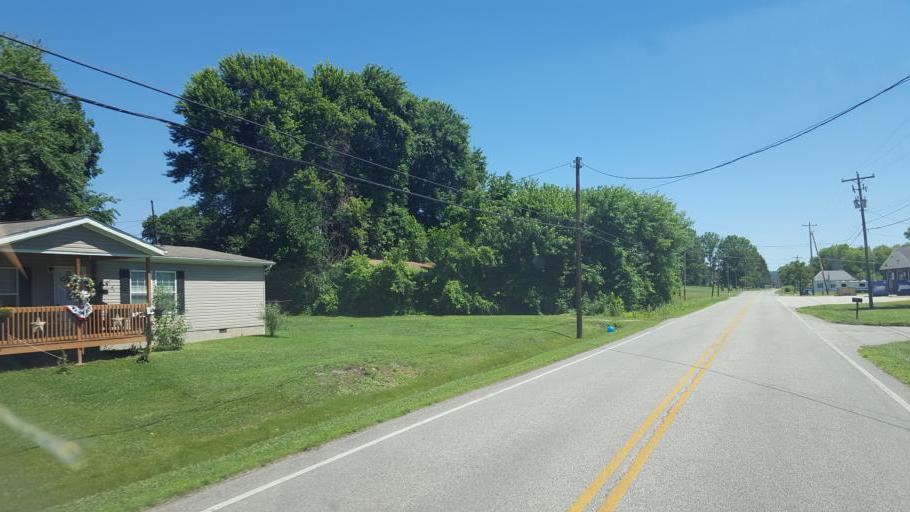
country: US
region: West Virginia
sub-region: Cabell County
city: Pea Ridge
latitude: 38.4489
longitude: -82.3303
